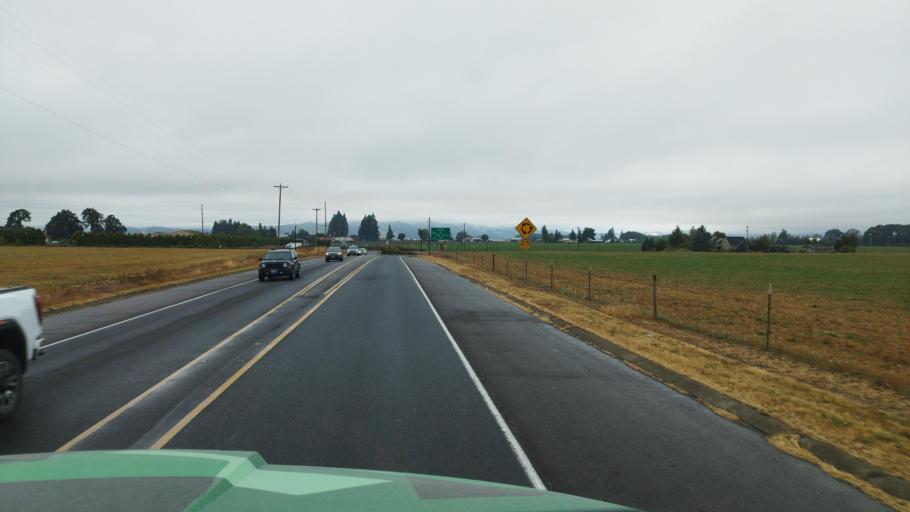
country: US
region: Oregon
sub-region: Washington County
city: Cornelius
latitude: 45.5514
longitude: -123.0696
